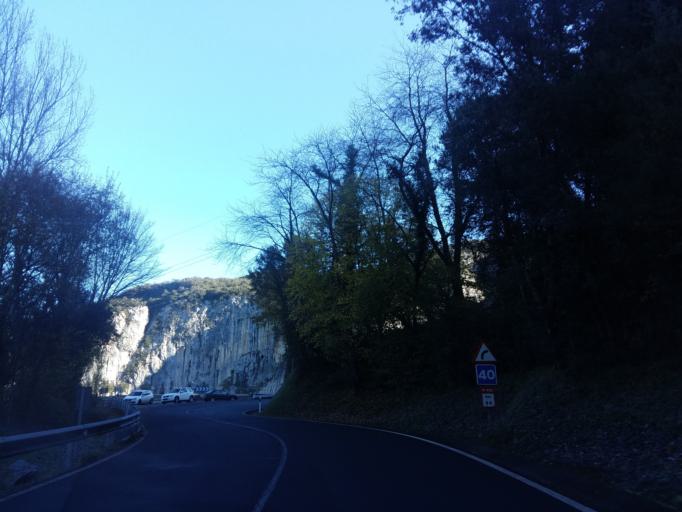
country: ES
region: Cantabria
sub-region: Provincia de Cantabria
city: Ramales de la Victoria
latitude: 43.2446
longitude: -3.4576
